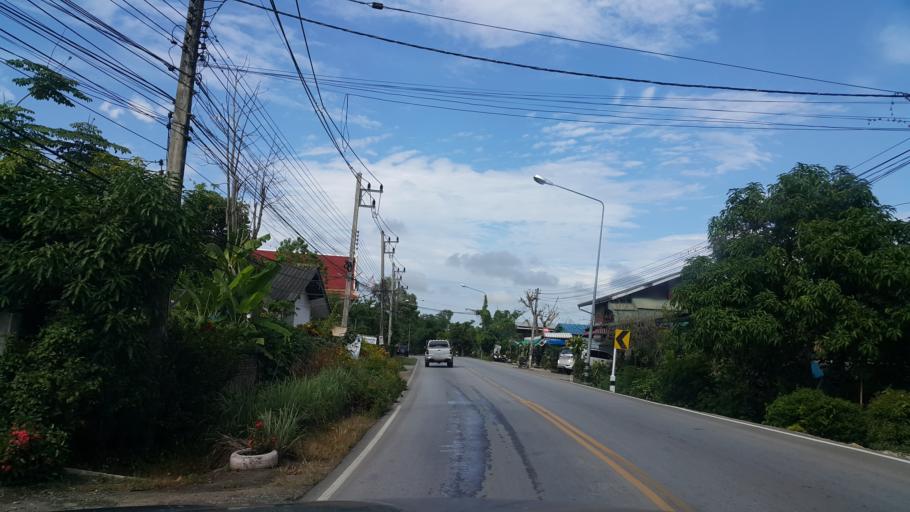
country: TH
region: Chiang Rai
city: Chiang Rai
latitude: 19.9108
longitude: 99.8793
